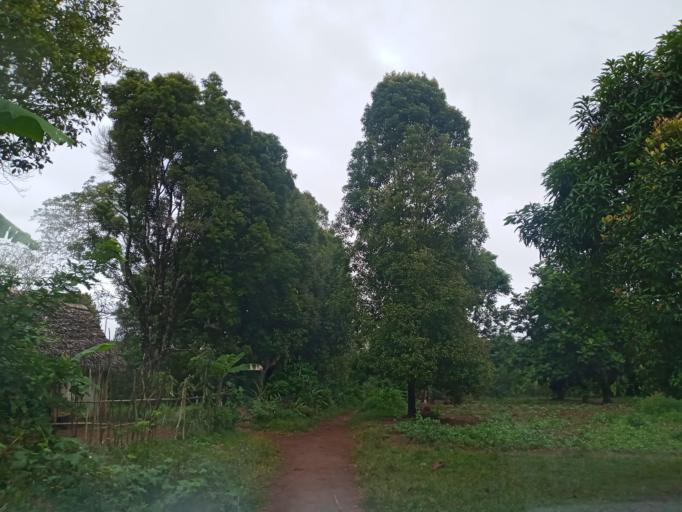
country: MG
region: Atsimo-Atsinanana
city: Vohipaho
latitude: -23.8273
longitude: 47.5442
